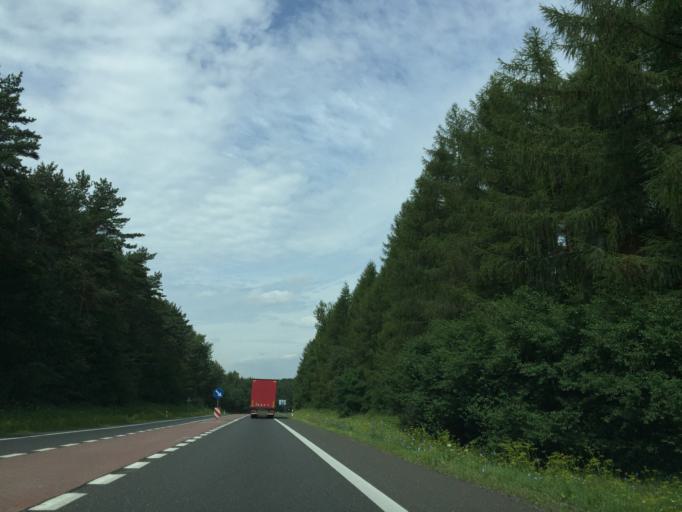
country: PL
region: Lesser Poland Voivodeship
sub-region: Powiat olkuski
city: Osiek
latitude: 50.2570
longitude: 19.6357
